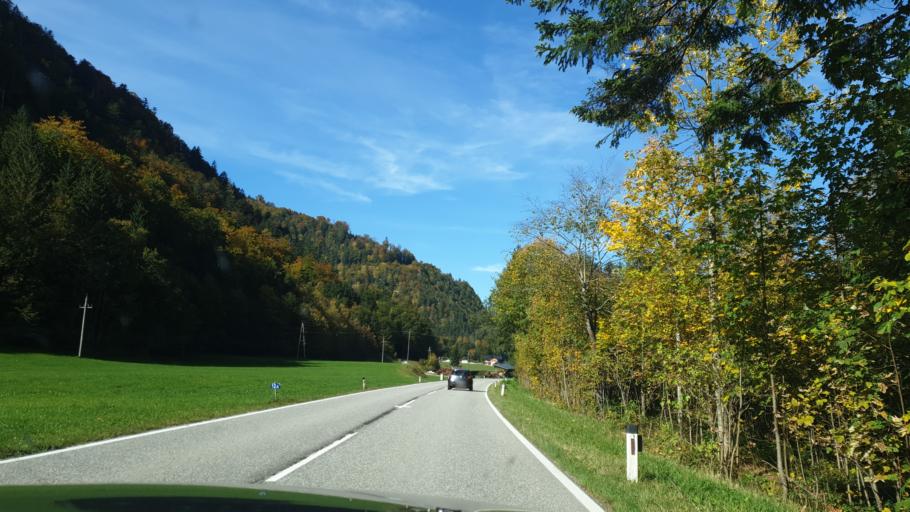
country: AT
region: Salzburg
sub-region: Politischer Bezirk Salzburg-Umgebung
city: Hintersee
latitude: 47.7199
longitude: 13.2819
